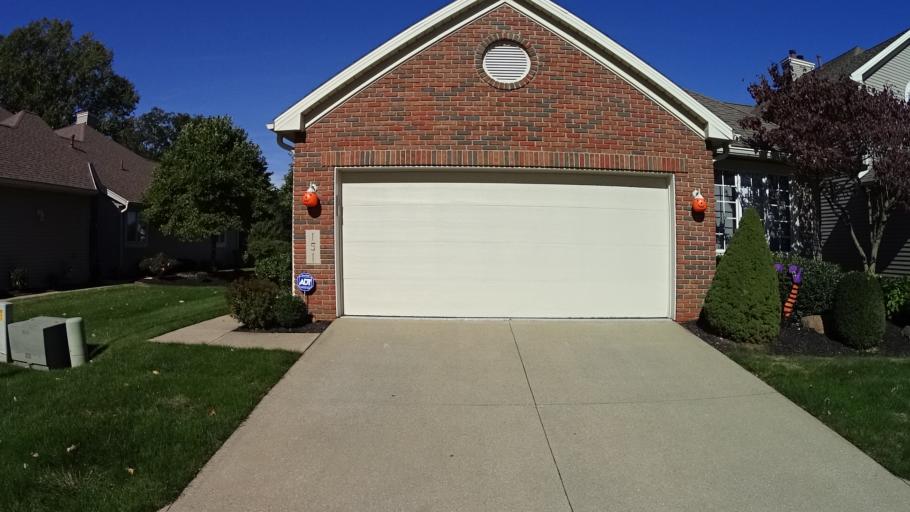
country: US
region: Ohio
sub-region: Lorain County
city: Amherst
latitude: 41.3849
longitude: -82.2233
